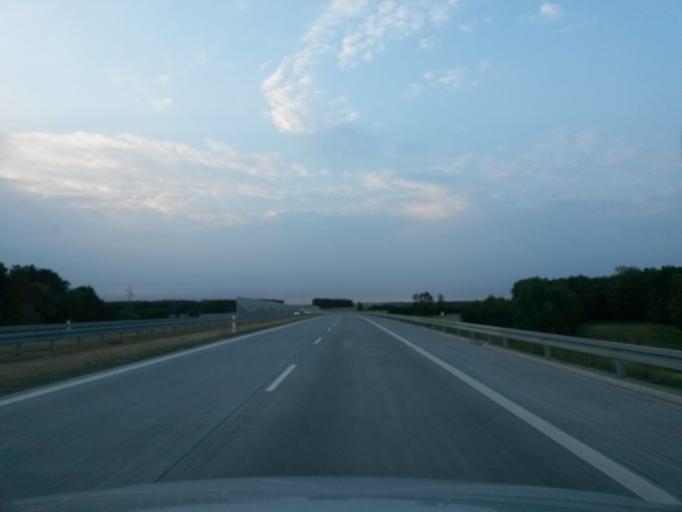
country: PL
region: Lodz Voivodeship
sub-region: Powiat sieradzki
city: Brzeznio
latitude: 51.5085
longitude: 18.6923
